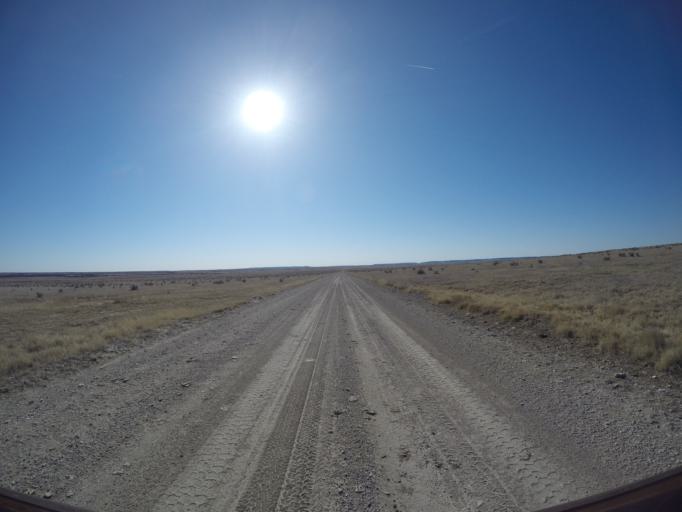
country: US
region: Colorado
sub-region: Otero County
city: La Junta
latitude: 37.7312
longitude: -103.6206
